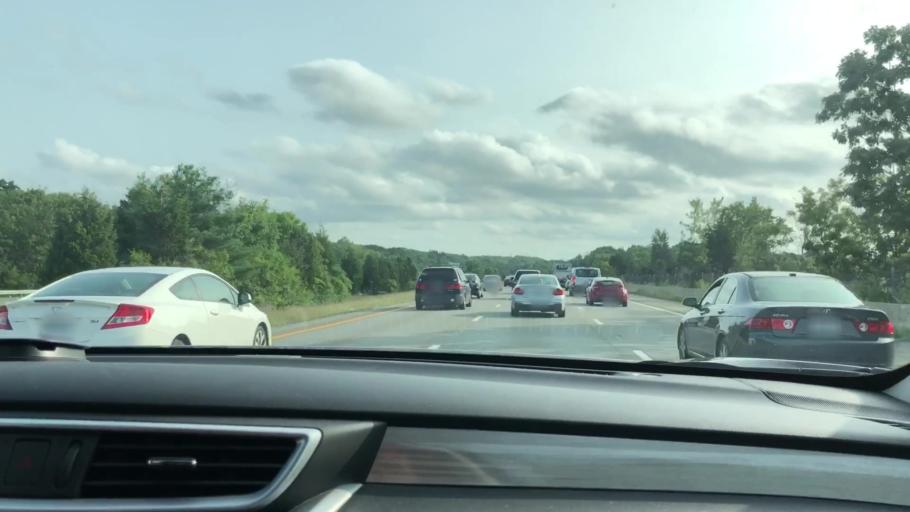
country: US
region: Massachusetts
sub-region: Bristol County
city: Attleboro
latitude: 41.9444
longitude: -71.3118
